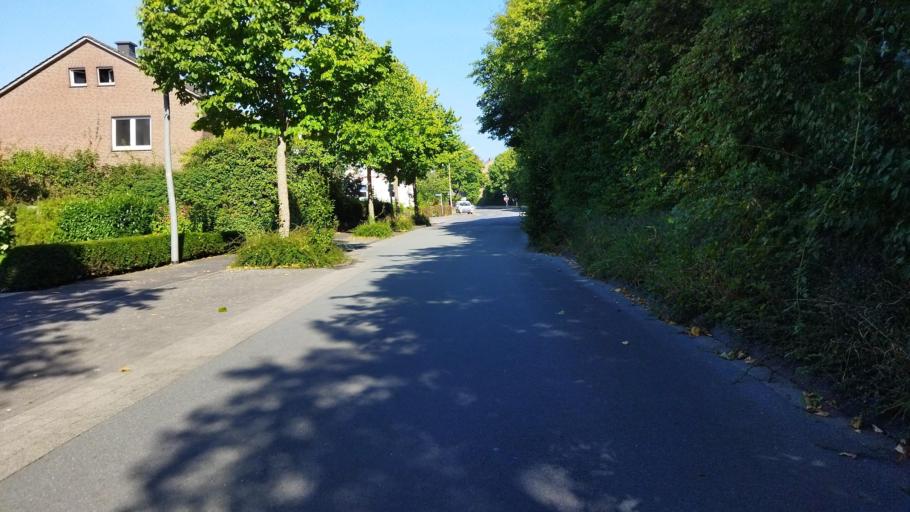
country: DE
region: North Rhine-Westphalia
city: Lengerich
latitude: 52.1805
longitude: 7.8712
